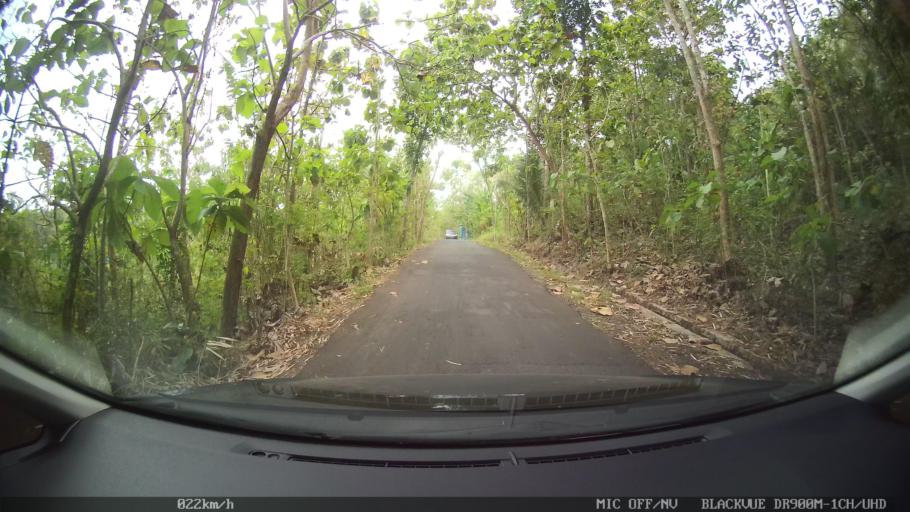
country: ID
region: Central Java
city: Candi Prambanan
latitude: -7.7991
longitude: 110.5208
